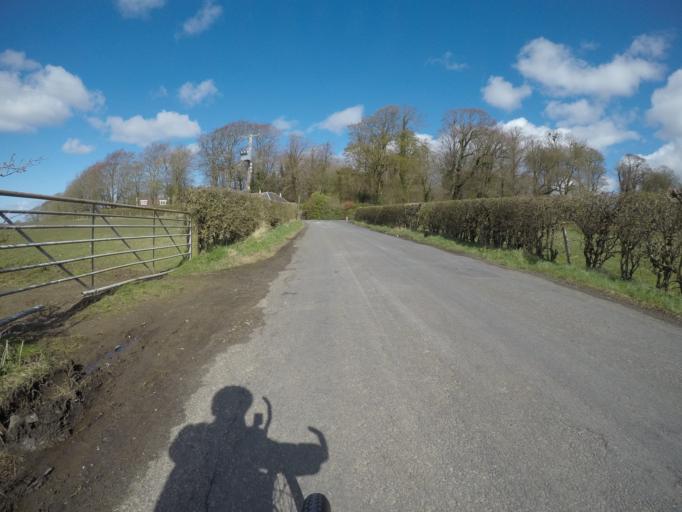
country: GB
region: Scotland
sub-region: East Ayrshire
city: Crosshouse
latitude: 55.6109
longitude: -4.5755
